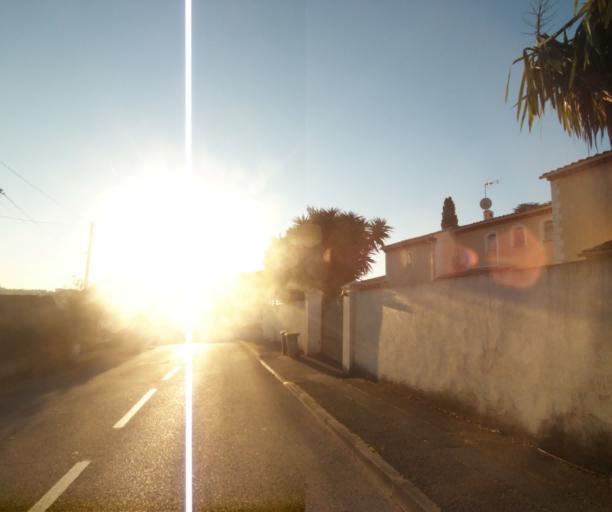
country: FR
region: Provence-Alpes-Cote d'Azur
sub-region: Departement des Alpes-Maritimes
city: Vallauris
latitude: 43.5792
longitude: 7.0854
